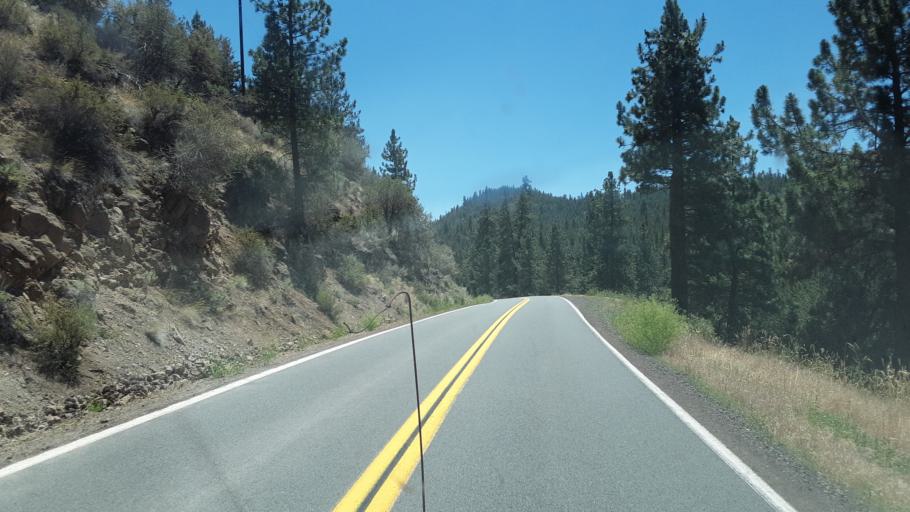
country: US
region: California
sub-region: Modoc County
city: Alturas
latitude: 41.0315
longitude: -120.8542
